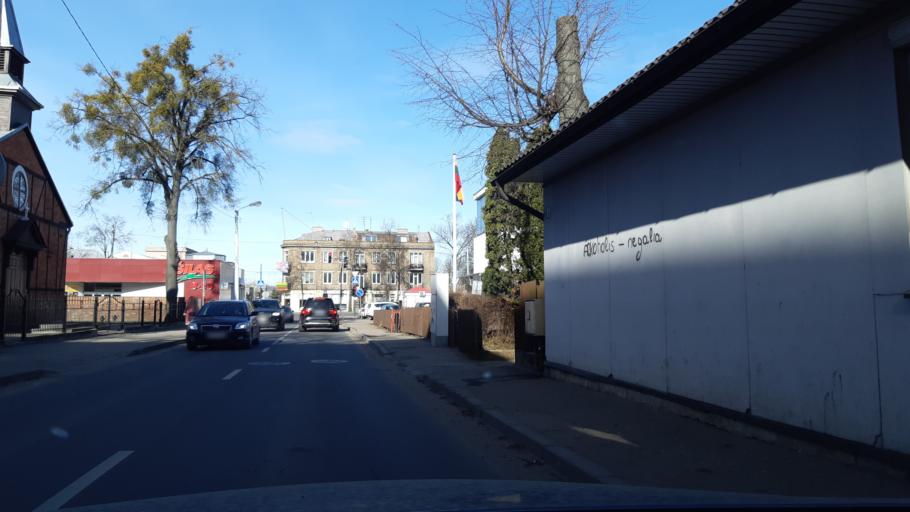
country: LT
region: Kauno apskritis
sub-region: Kaunas
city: Kaunas
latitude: 54.9050
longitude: 23.9216
